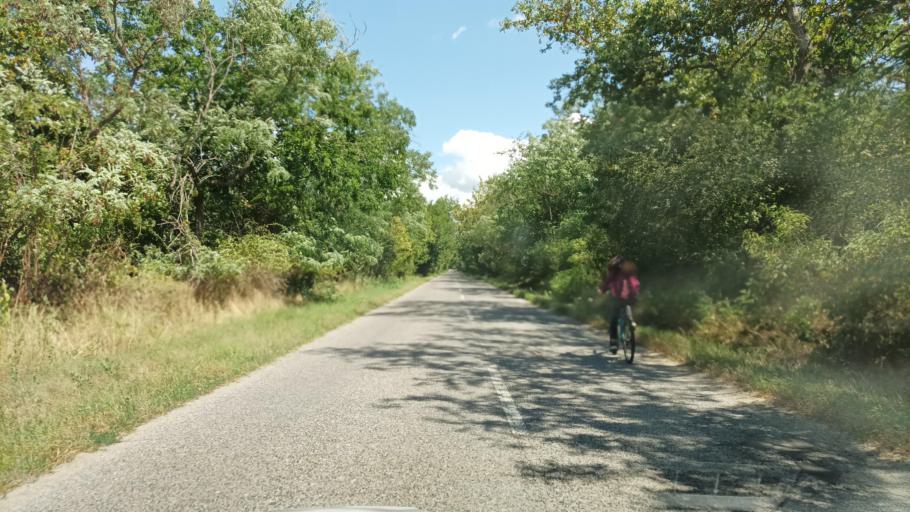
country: HU
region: Pest
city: Szentendre
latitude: 47.6763
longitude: 19.0911
